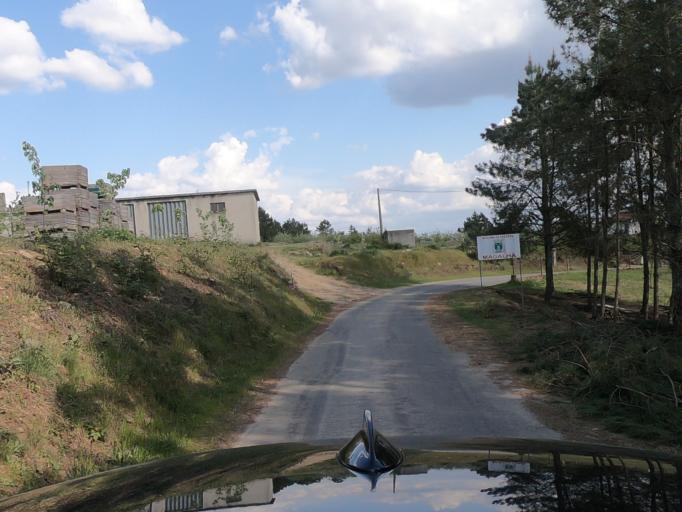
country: PT
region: Vila Real
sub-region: Sabrosa
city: Vilela
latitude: 41.2448
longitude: -7.6606
